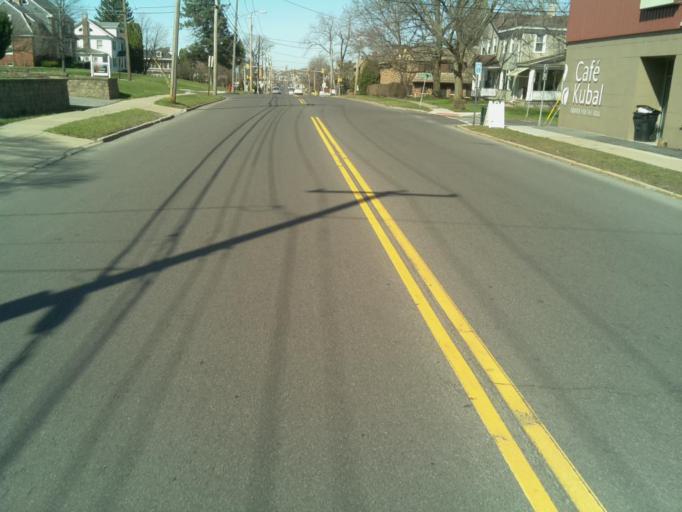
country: US
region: New York
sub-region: Onondaga County
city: East Syracuse
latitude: 43.0692
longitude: -76.0980
